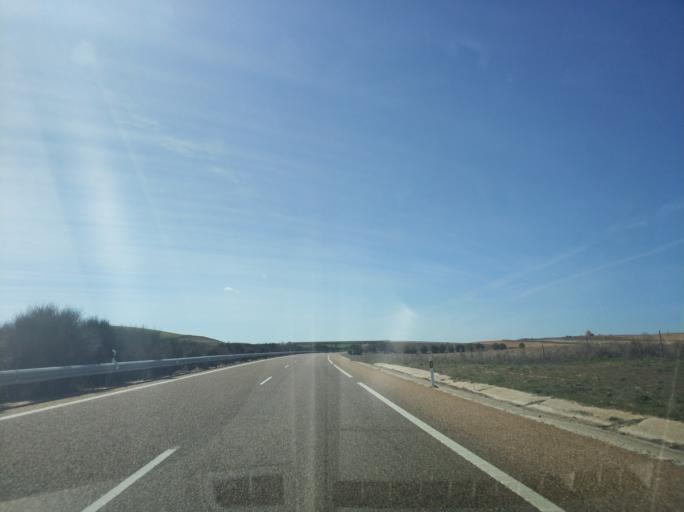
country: ES
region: Castille and Leon
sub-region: Provincia de Valladolid
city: Pollos
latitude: 41.4387
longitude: -5.0938
